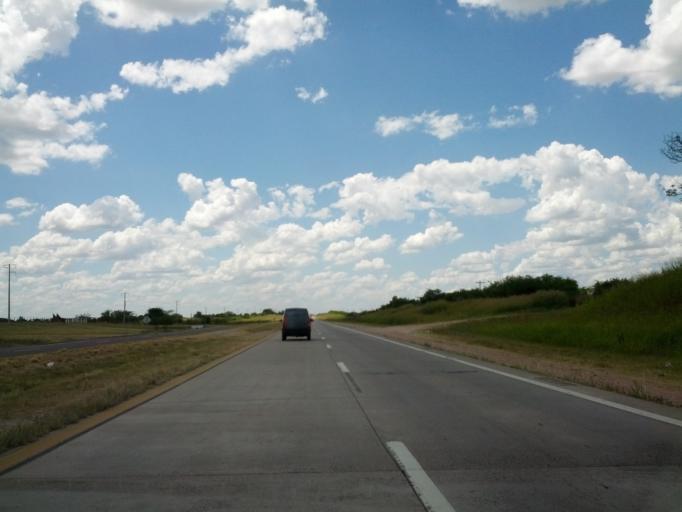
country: AR
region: Entre Rios
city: Gualeguaychu
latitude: -32.9423
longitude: -58.5767
